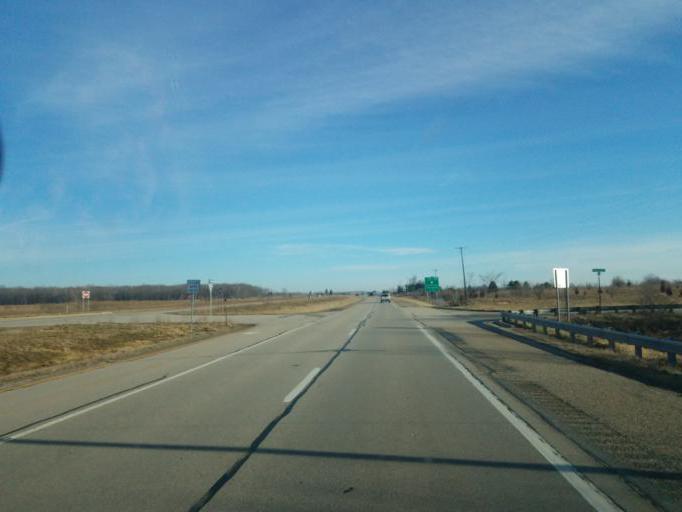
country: US
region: Michigan
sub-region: Gratiot County
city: Ithaca
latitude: 43.1610
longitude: -84.5632
